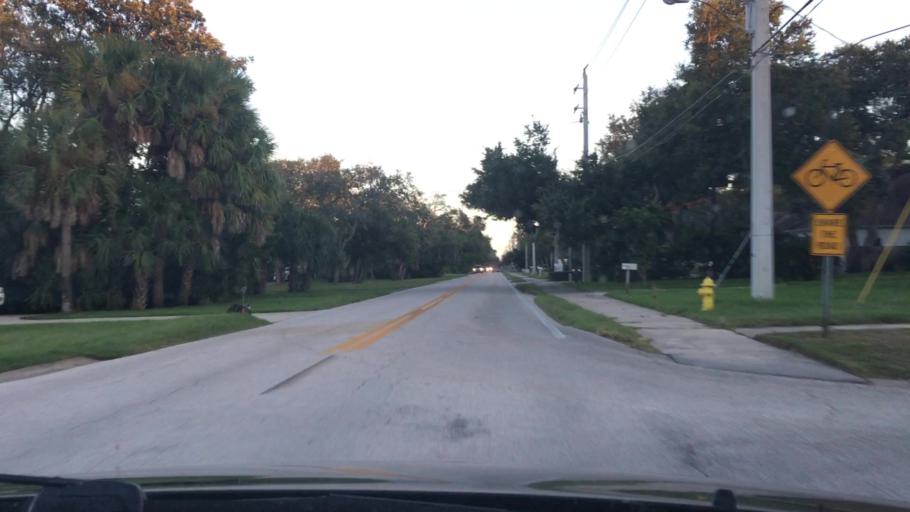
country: US
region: Florida
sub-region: Volusia County
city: Ormond Beach
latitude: 29.3124
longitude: -81.0690
